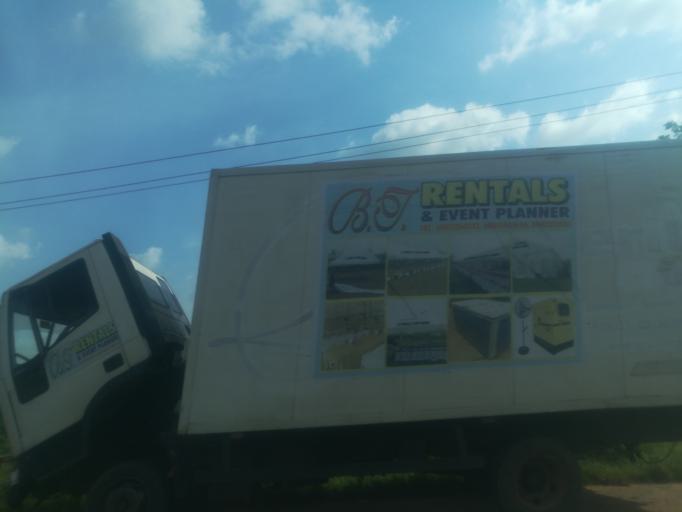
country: NG
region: Oyo
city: Ido
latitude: 7.3968
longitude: 3.7940
